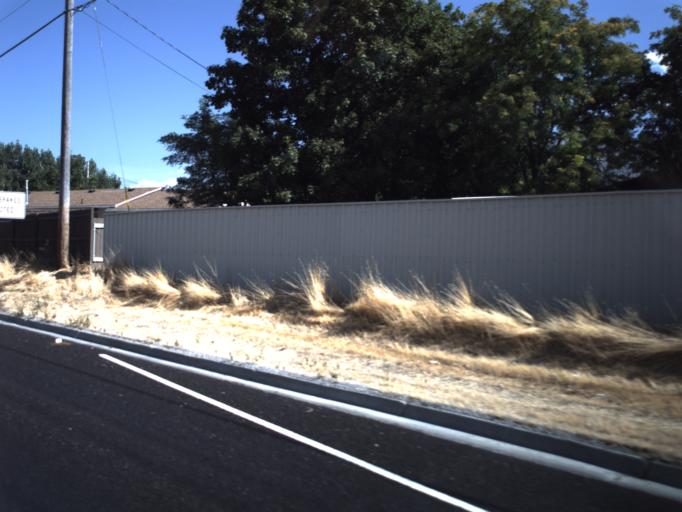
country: US
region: Utah
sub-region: Cache County
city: Nibley
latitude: 41.6573
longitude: -111.8327
